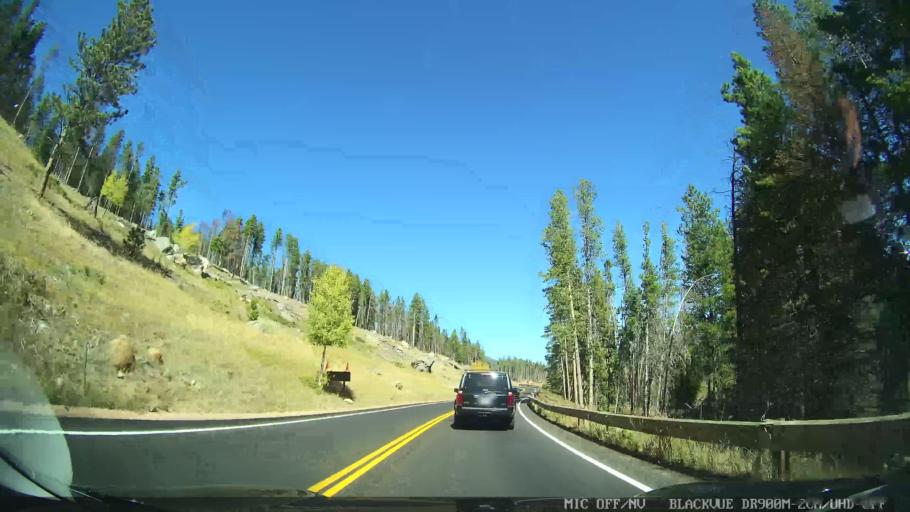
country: US
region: Colorado
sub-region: Larimer County
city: Estes Park
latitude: 40.3319
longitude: -105.5996
